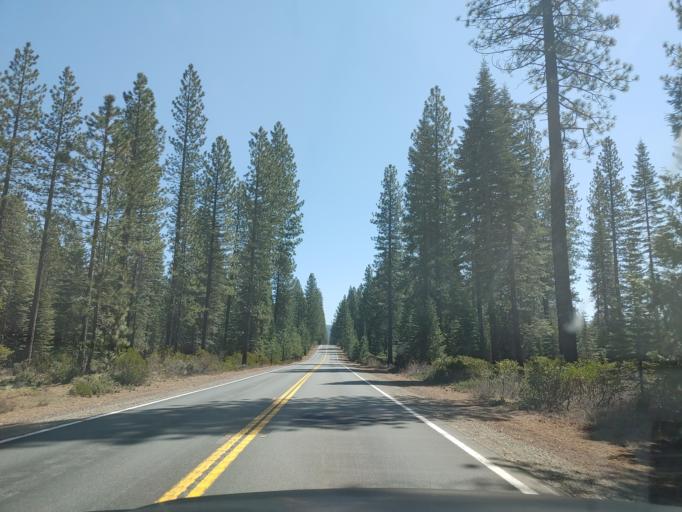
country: US
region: California
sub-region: Siskiyou County
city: McCloud
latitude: 41.2590
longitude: -121.8391
